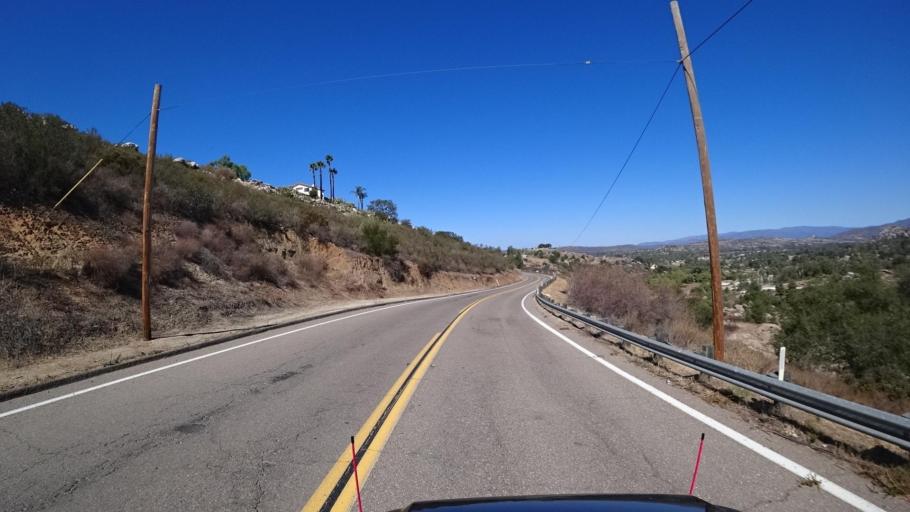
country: US
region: California
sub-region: San Diego County
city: Ramona
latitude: 33.0399
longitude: -116.8384
